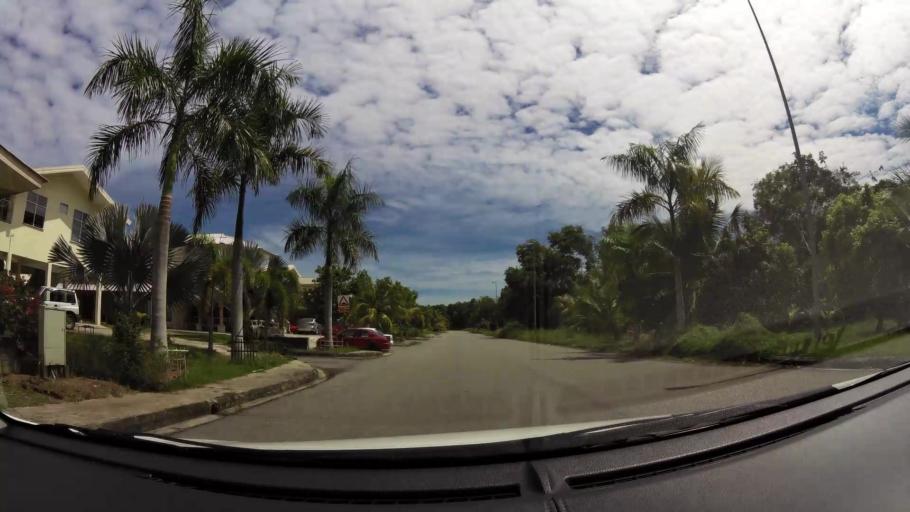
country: BN
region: Brunei and Muara
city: Bandar Seri Begawan
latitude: 4.9926
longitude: 115.0117
